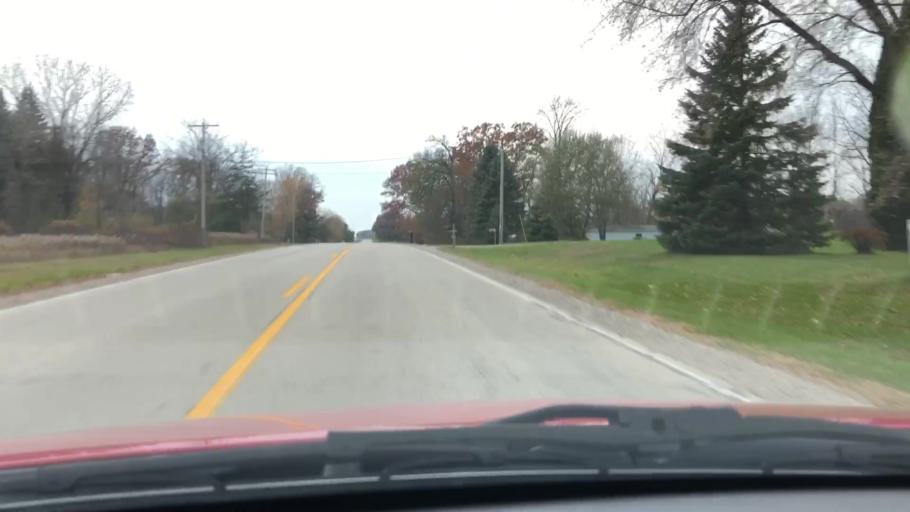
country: US
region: Wisconsin
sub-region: Brown County
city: Oneida
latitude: 44.4443
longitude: -88.2376
